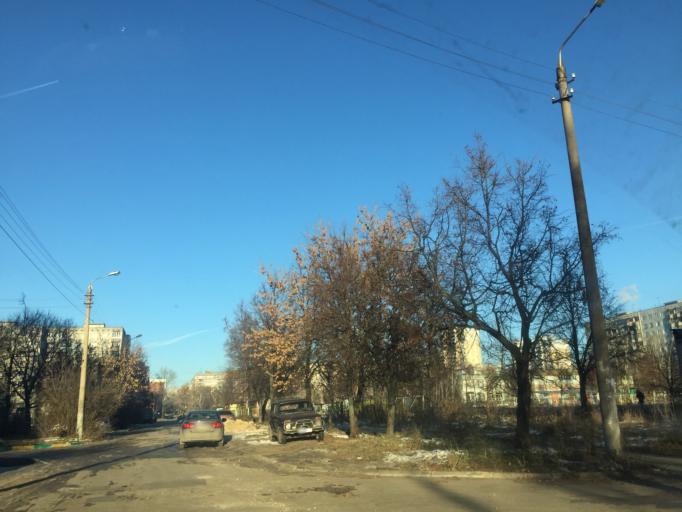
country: RU
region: Tula
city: Tula
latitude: 54.2100
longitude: 37.5985
